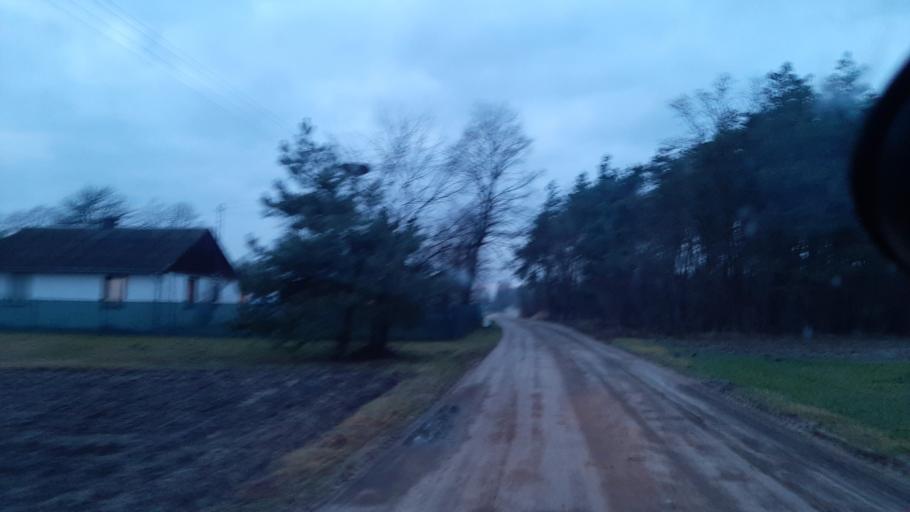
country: PL
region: Lublin Voivodeship
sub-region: Powiat lubartowski
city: Firlej
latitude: 51.5899
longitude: 22.5344
